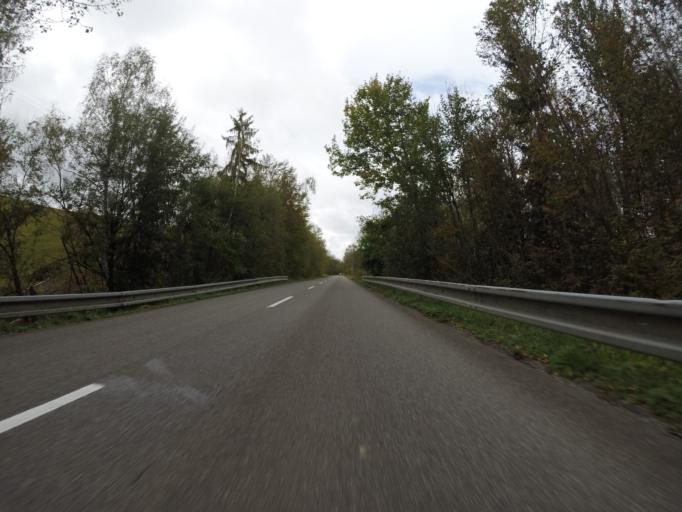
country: SK
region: Banskobystricky
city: Poltar
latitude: 48.5883
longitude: 19.7480
